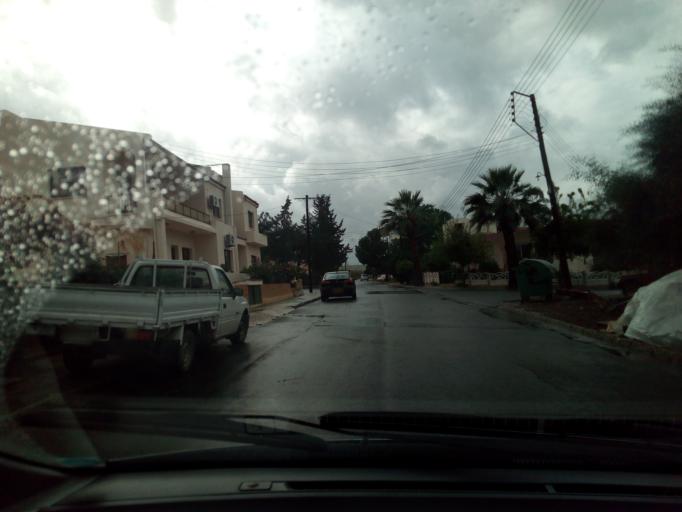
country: CY
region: Pafos
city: Polis
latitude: 35.0662
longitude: 32.4863
